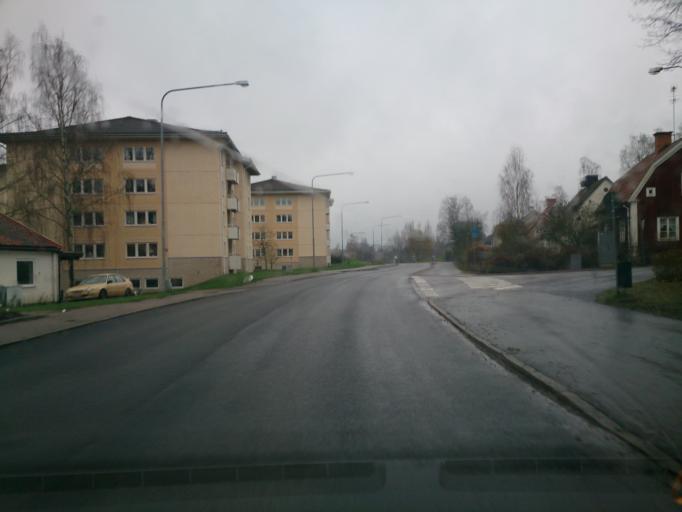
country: SE
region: OEstergoetland
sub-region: Atvidabergs Kommun
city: Atvidaberg
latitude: 58.2048
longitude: 16.0077
